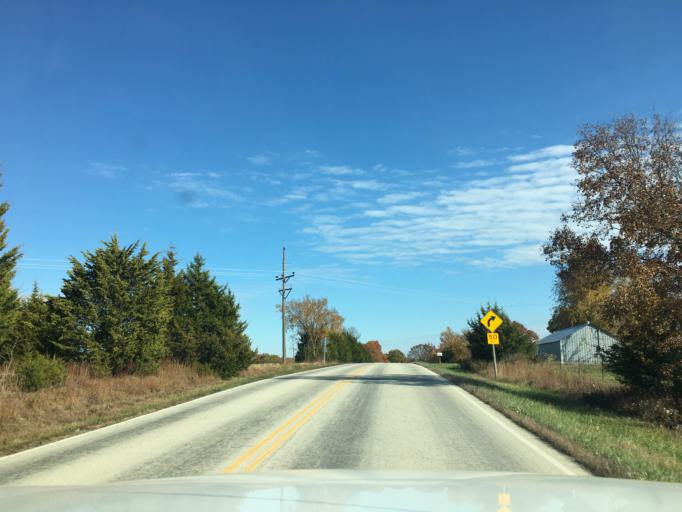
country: US
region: Missouri
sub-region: Maries County
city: Belle
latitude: 38.3038
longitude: -91.7316
